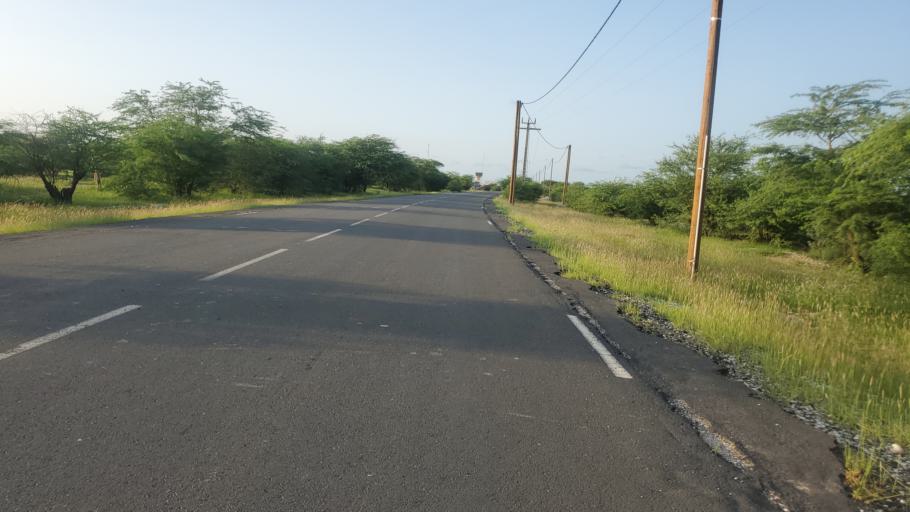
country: SN
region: Saint-Louis
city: Saint-Louis
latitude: 16.2089
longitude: -16.4155
